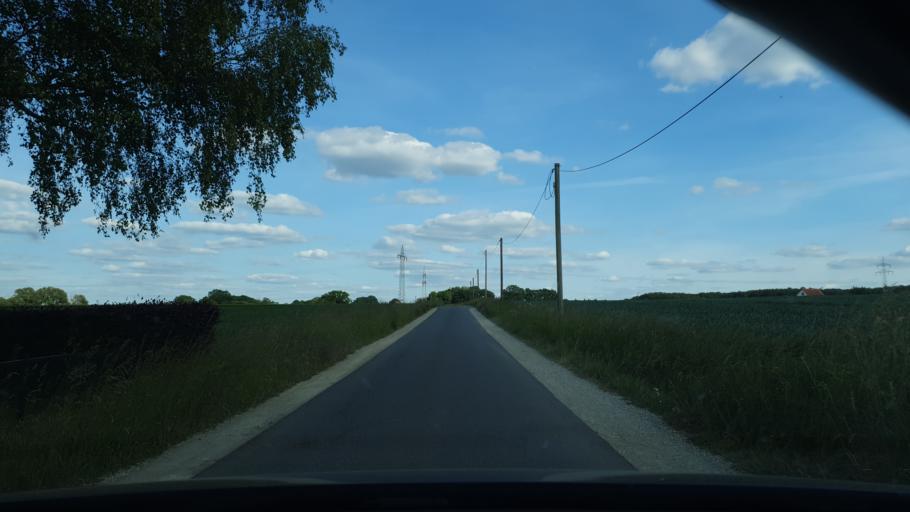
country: DE
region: North Rhine-Westphalia
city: Enger
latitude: 52.1674
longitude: 8.5358
